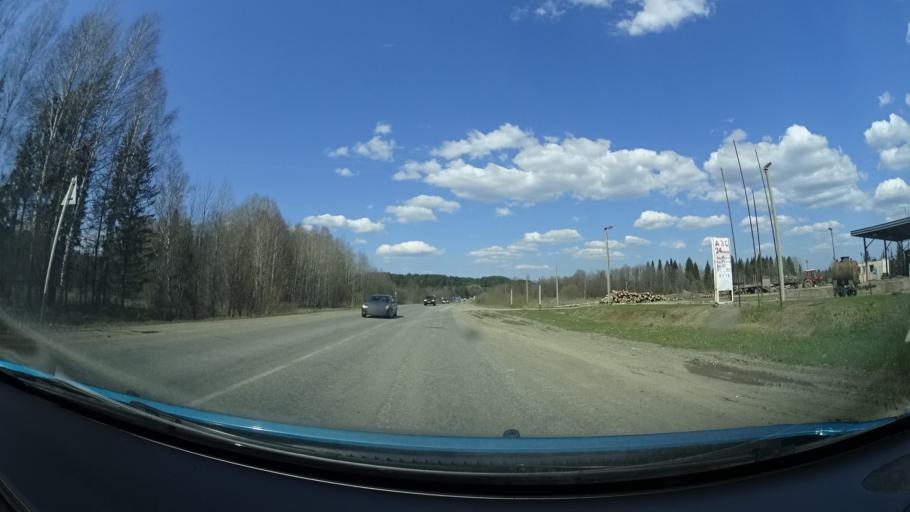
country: RU
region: Perm
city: Yugo-Kamskiy
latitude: 57.5404
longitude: 55.6862
